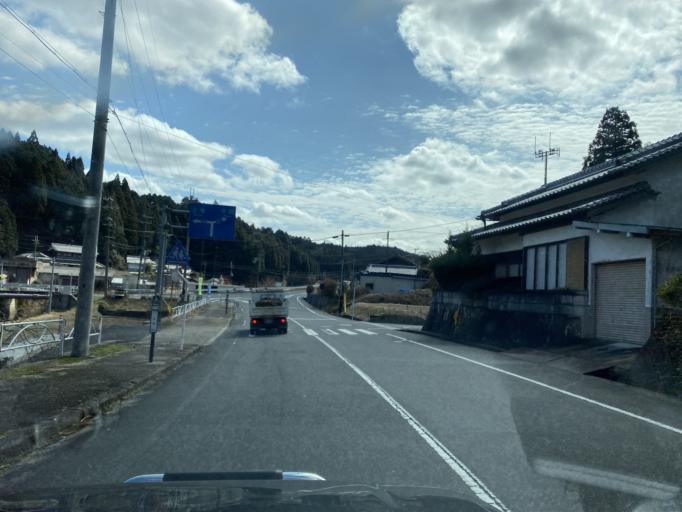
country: JP
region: Nara
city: Haibara-akanedai
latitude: 34.6751
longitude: 135.9500
